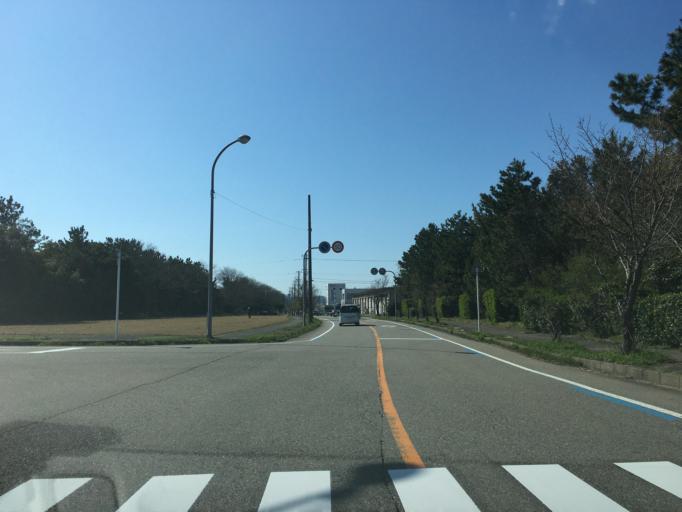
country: JP
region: Toyama
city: Nishishinminato
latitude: 36.7796
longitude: 137.0994
